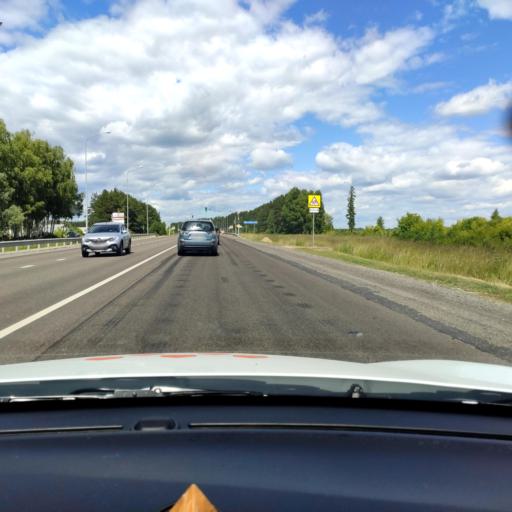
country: RU
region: Mariy-El
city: Pomary
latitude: 55.9189
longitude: 48.3711
